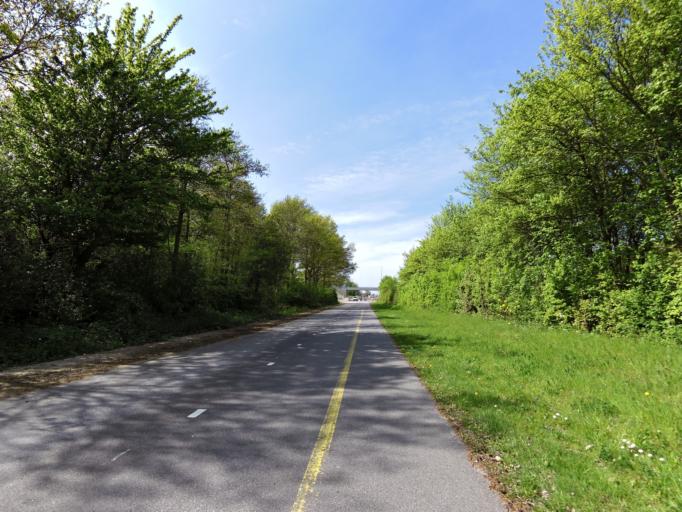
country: NL
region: South Holland
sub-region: Gemeente Brielle
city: Brielle
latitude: 51.8889
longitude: 4.1990
